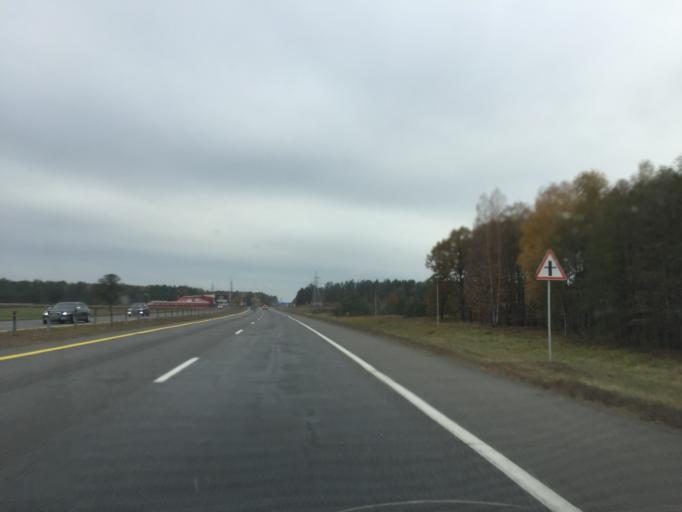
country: BY
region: Gomel
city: Horad Rechytsa
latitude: 52.3359
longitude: 30.5474
